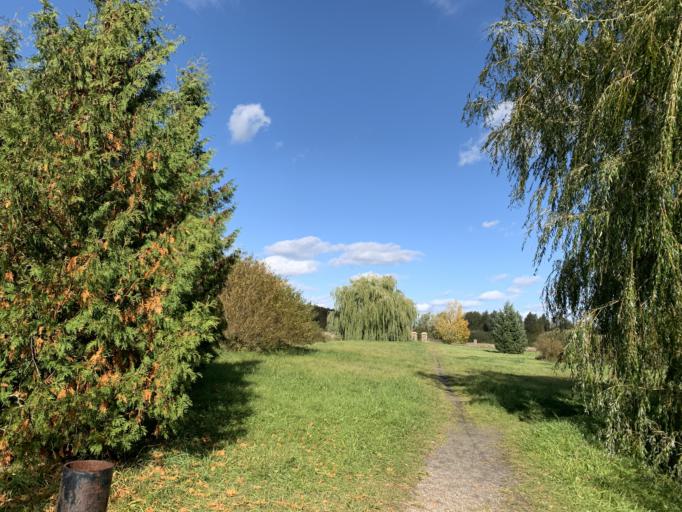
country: BY
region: Minsk
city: Nyasvizh
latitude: 53.2279
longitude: 26.7035
